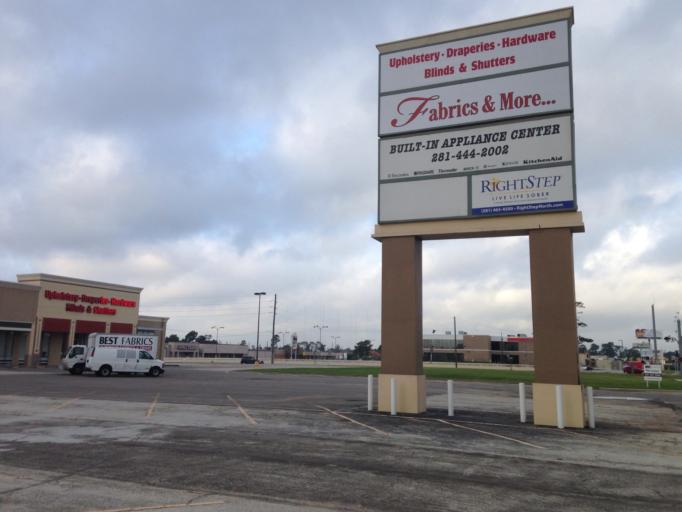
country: US
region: Texas
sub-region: Harris County
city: Spring
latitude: 30.0074
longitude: -95.4624
